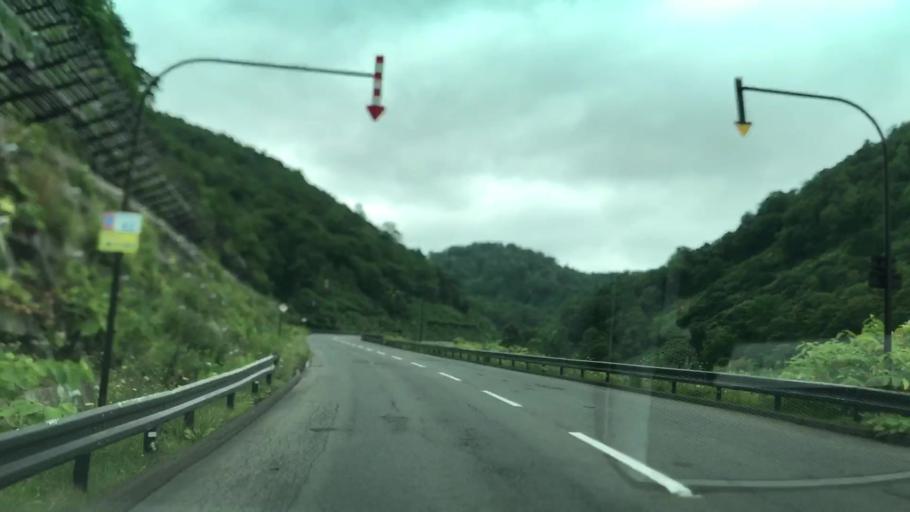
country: JP
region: Hokkaido
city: Yoichi
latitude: 42.9866
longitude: 140.8722
